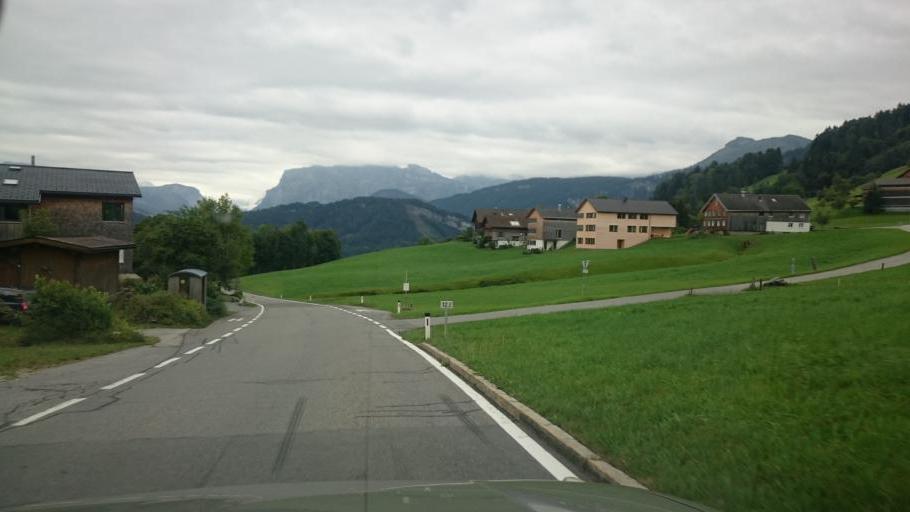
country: AT
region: Vorarlberg
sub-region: Politischer Bezirk Bregenz
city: Andelsbuch
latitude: 47.4175
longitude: 9.8410
